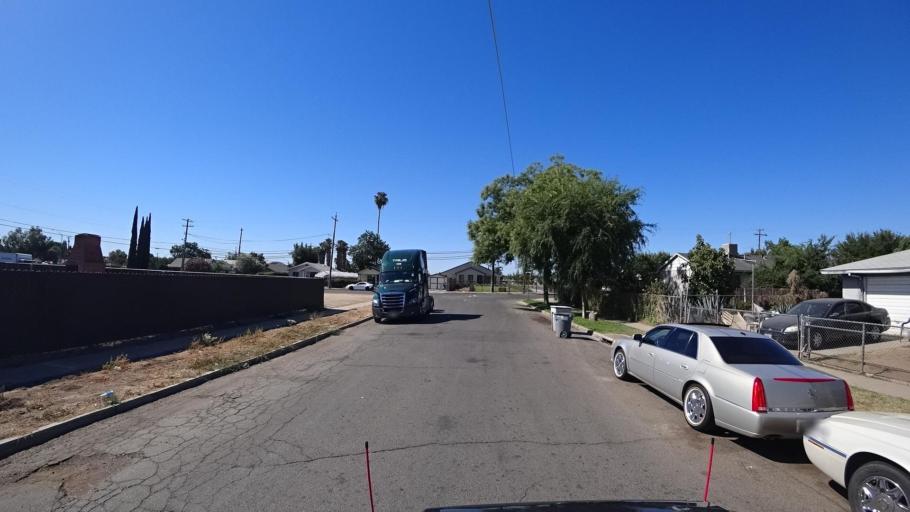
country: US
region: California
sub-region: Fresno County
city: Fresno
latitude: 36.7183
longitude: -119.7919
